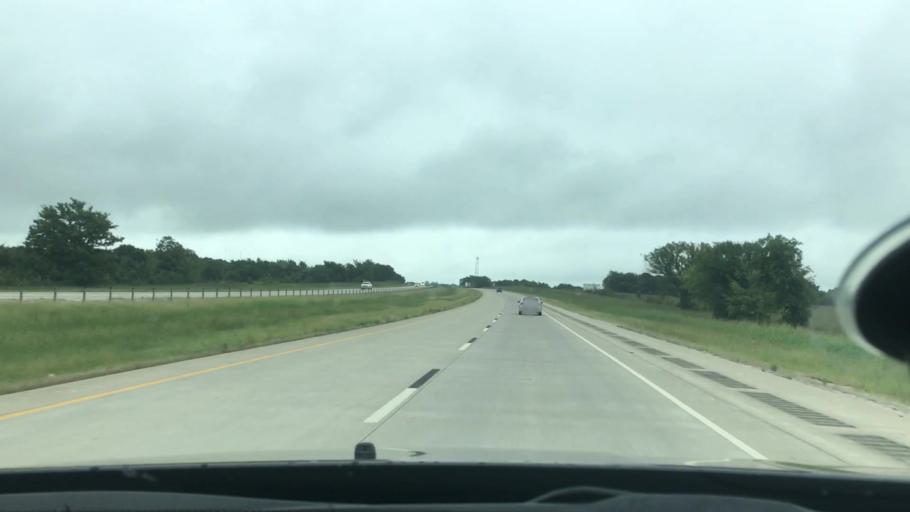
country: US
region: Oklahoma
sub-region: Okmulgee County
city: Henryetta
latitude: 35.4274
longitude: -96.0677
